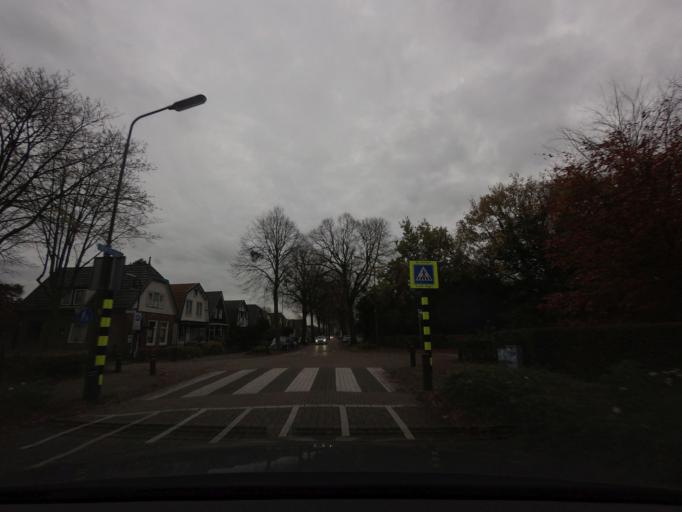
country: NL
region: North Holland
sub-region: Gemeente Heiloo
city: Heiloo
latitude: 52.5993
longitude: 4.7061
